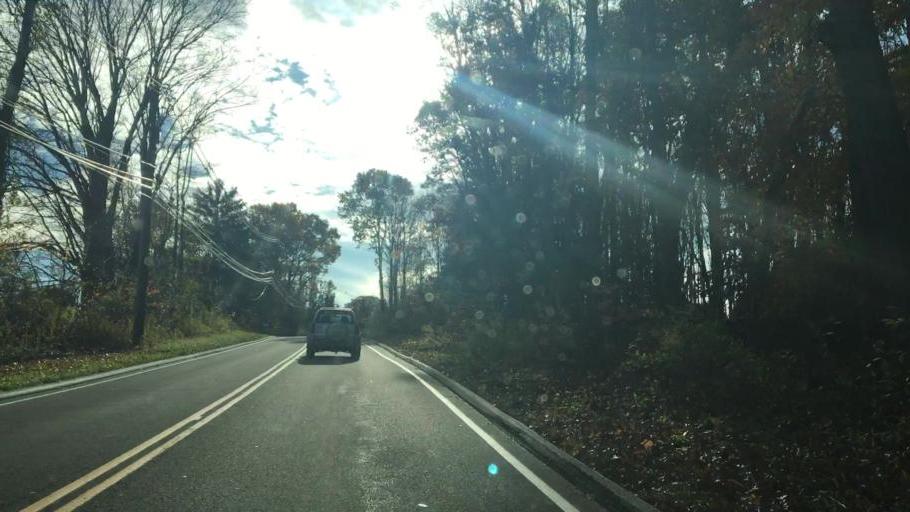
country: US
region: Connecticut
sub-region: New Haven County
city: Ansonia
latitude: 41.3724
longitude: -73.1232
